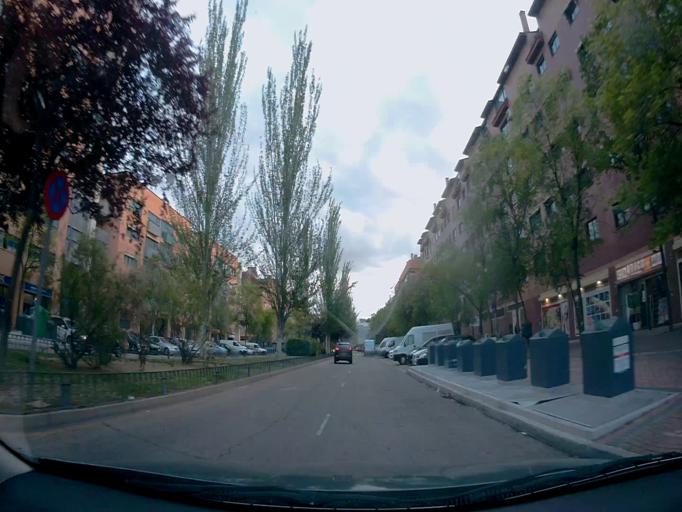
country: ES
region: Madrid
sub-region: Provincia de Madrid
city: Alcorcon
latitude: 40.3479
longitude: -3.8412
